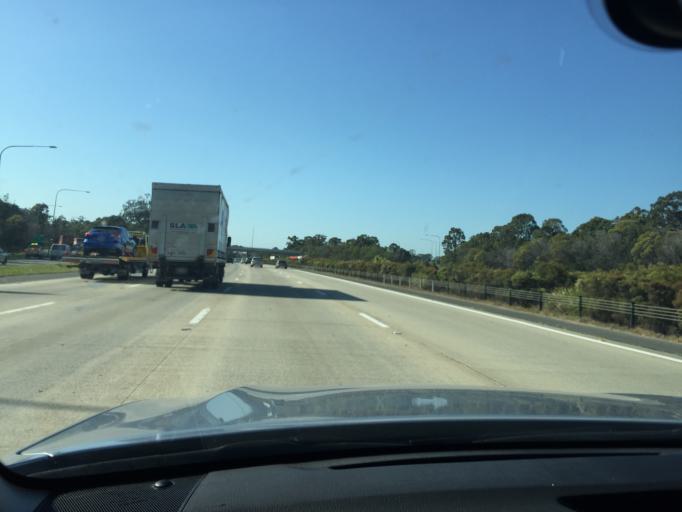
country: AU
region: Queensland
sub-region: Gold Coast
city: Ormeau Hills
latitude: -27.7562
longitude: 153.2399
